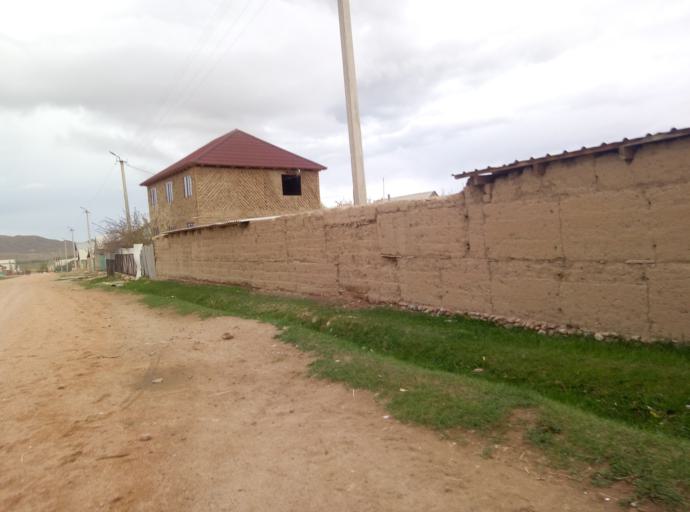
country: KG
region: Ysyk-Koel
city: Bokombayevskoye
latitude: 42.1107
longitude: 76.9790
